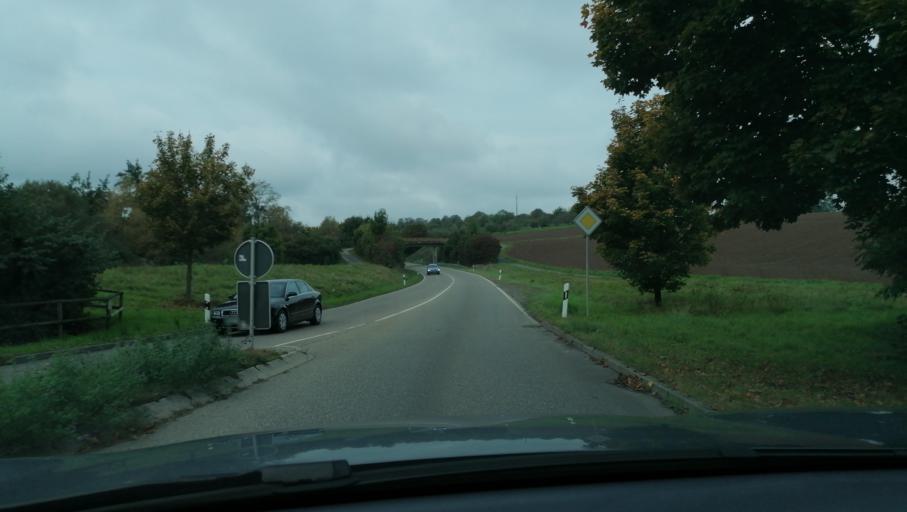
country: DE
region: Baden-Wuerttemberg
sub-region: Regierungsbezirk Stuttgart
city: Winnenden
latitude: 48.8668
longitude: 9.4187
